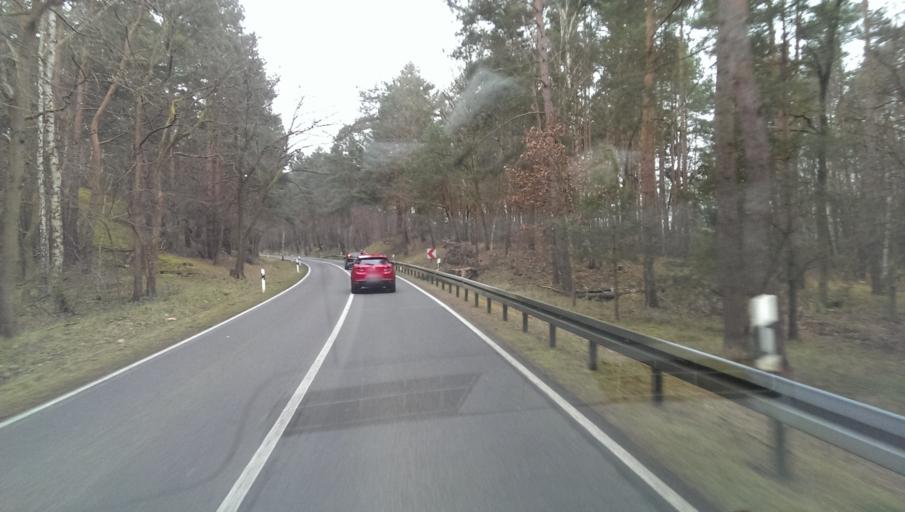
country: DE
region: Brandenburg
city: Grossbeeren
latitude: 52.3269
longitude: 13.3001
